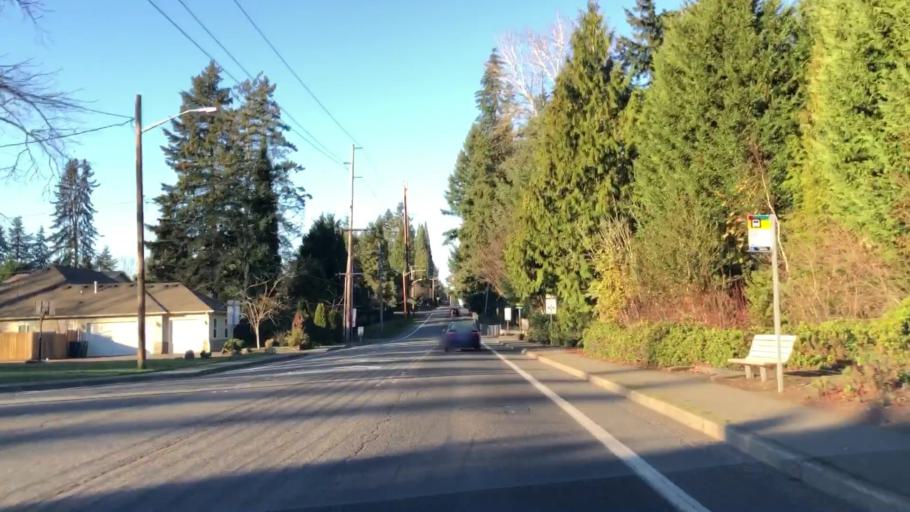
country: US
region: Washington
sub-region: King County
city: Sammamish
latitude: 47.6313
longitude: -122.1099
